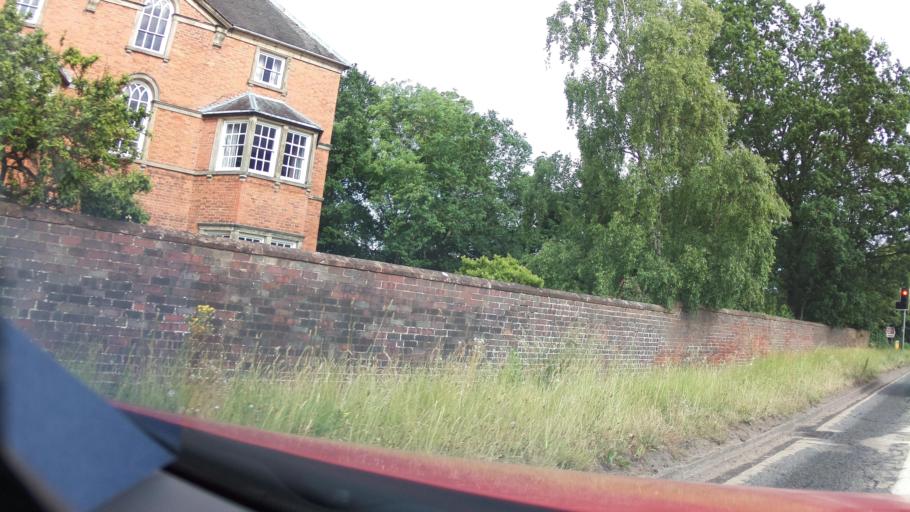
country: GB
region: England
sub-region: Dudley
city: Kingswinford
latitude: 52.5178
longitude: -2.1747
